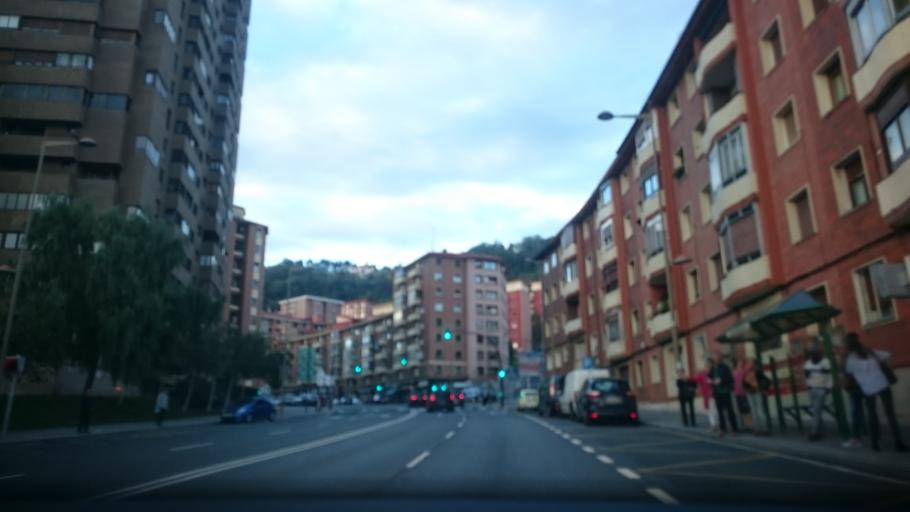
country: ES
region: Basque Country
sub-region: Bizkaia
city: Bilbao
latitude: 43.2653
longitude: -2.9168
